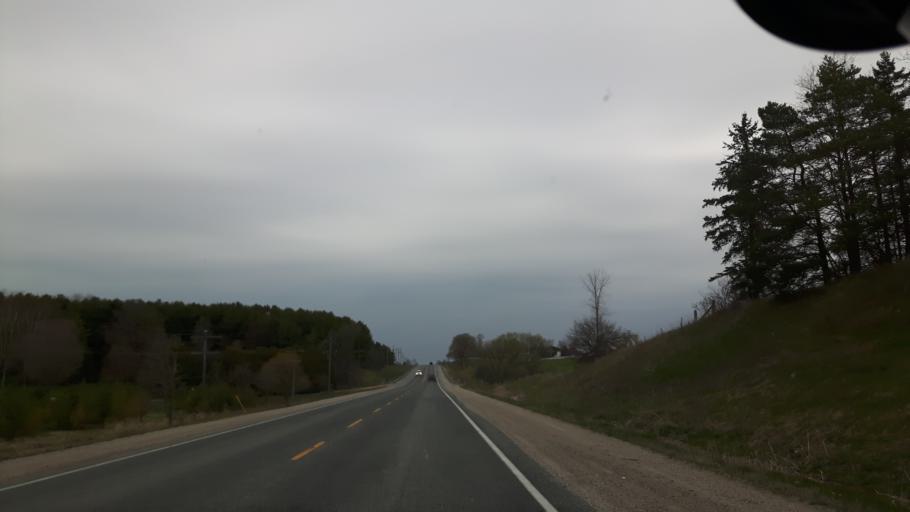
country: CA
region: Ontario
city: Goderich
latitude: 43.6688
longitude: -81.6222
